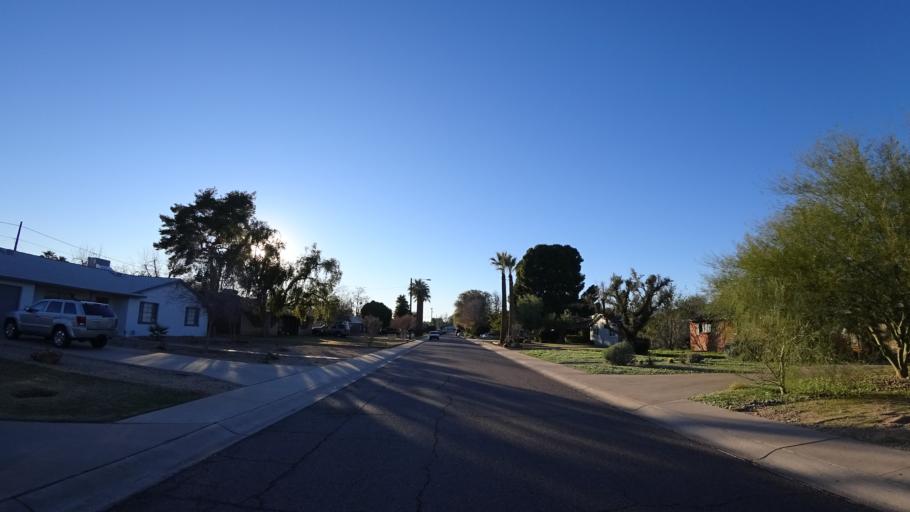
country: US
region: Arizona
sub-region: Maricopa County
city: Phoenix
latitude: 33.4866
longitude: -112.0330
